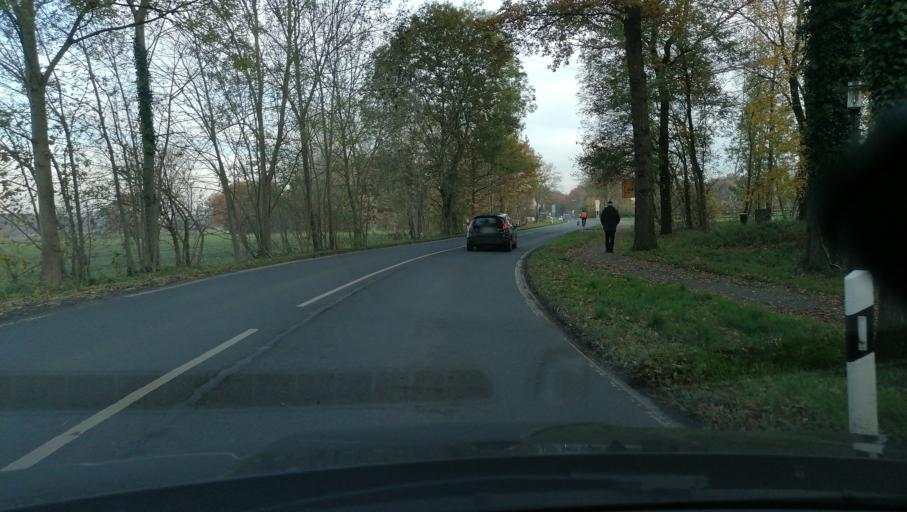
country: DE
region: North Rhine-Westphalia
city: Castrop-Rauxel
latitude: 51.5798
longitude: 7.2691
